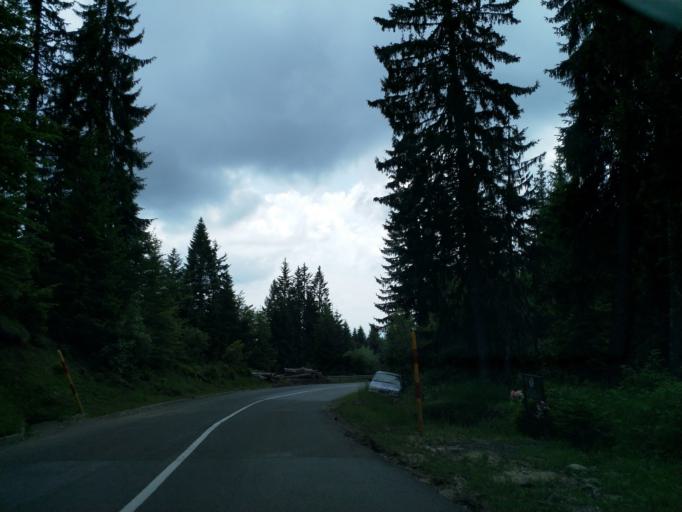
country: XK
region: Mitrovica
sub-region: Komuna e Leposaviqit
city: Leposaviq
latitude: 43.2754
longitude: 20.7912
